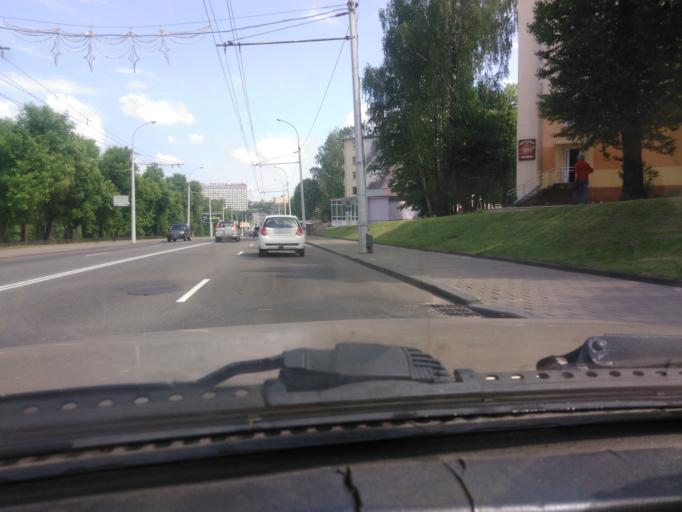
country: BY
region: Mogilev
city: Mahilyow
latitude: 53.9120
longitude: 30.3225
